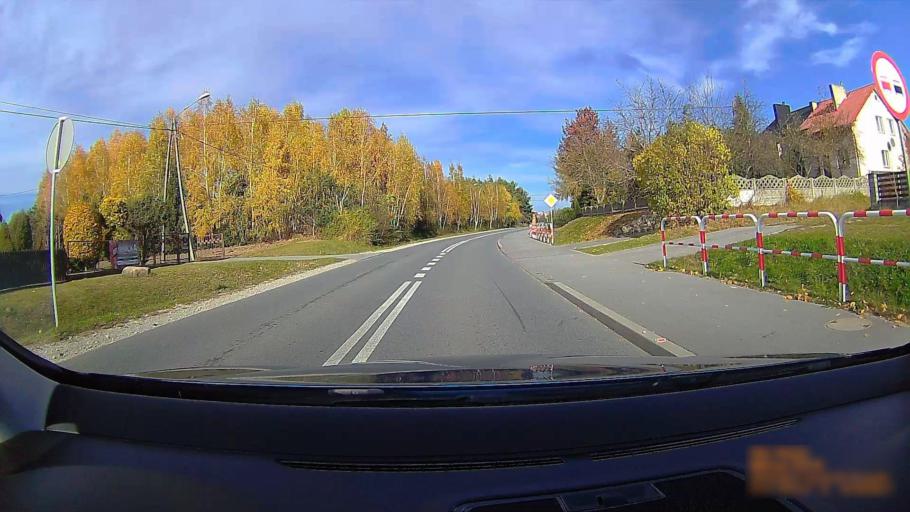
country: PL
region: Greater Poland Voivodeship
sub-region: Powiat kepinski
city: Kepno
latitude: 51.3227
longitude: 18.0134
